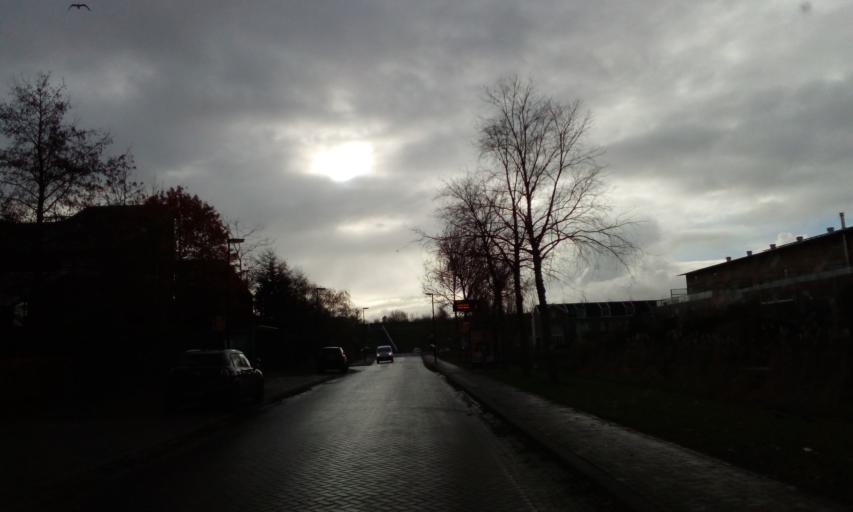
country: NL
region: South Holland
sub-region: Gemeente Lansingerland
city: Bergschenhoek
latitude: 51.9519
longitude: 4.5182
